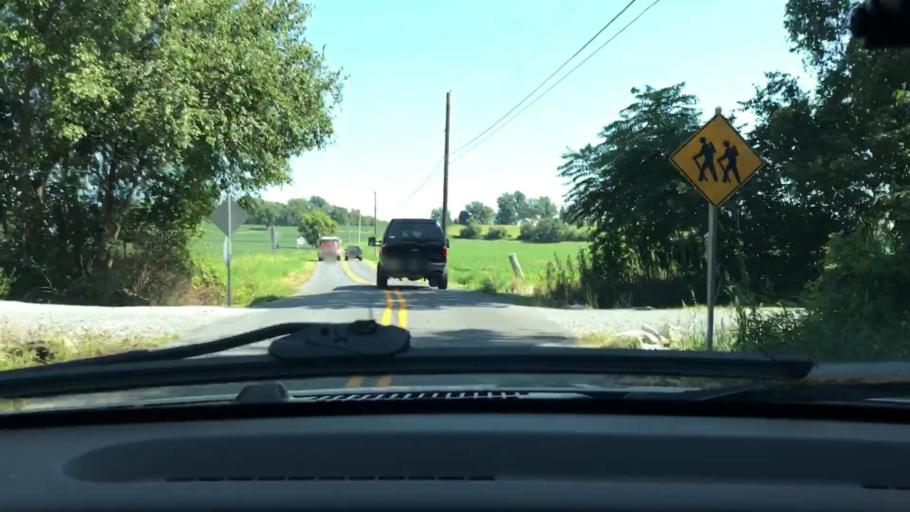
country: US
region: Pennsylvania
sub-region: Lancaster County
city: Elizabethtown
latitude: 40.1823
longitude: -76.6112
